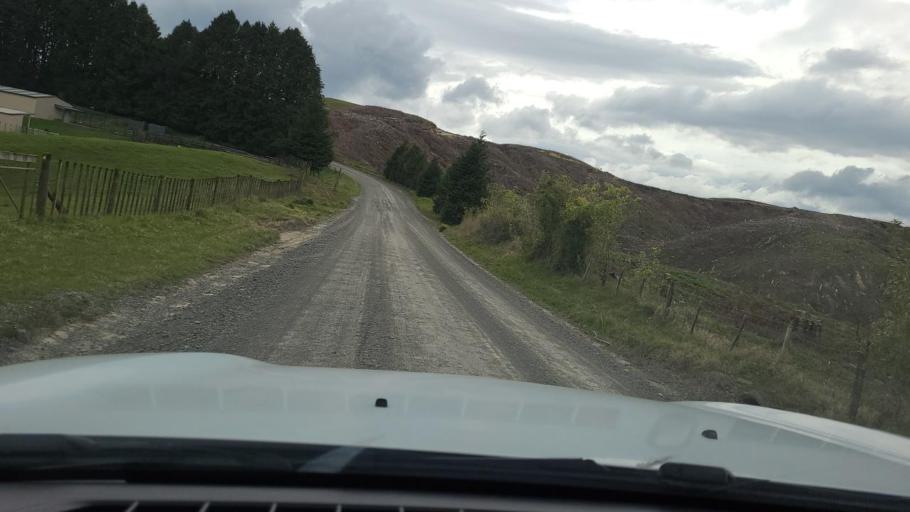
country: NZ
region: Hawke's Bay
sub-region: Napier City
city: Napier
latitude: -39.3123
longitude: 176.8361
